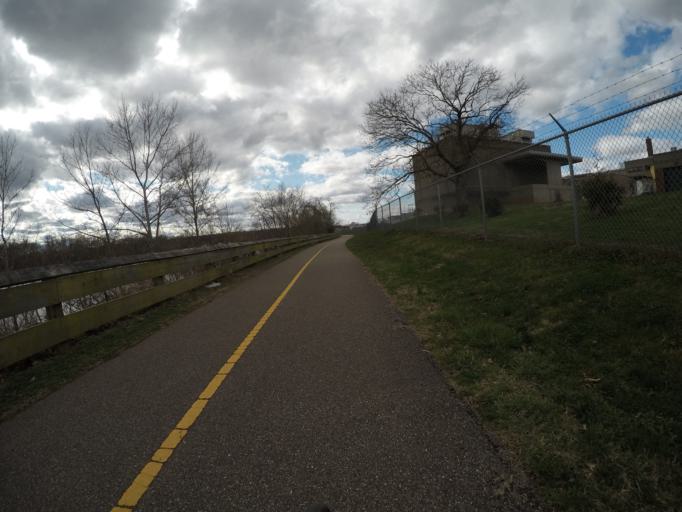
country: US
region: West Virginia
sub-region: Wood County
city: Williamstown
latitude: 39.4082
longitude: -81.4333
